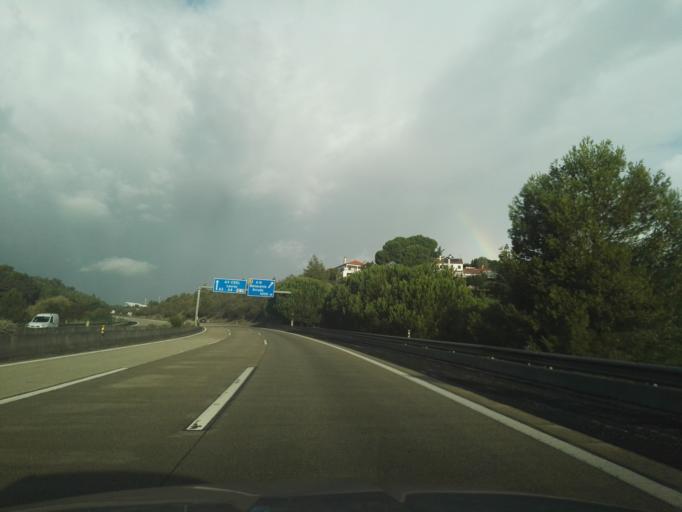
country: PT
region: Lisbon
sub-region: Vila Franca de Xira
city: Sobralinho
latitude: 38.9044
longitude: -9.0579
